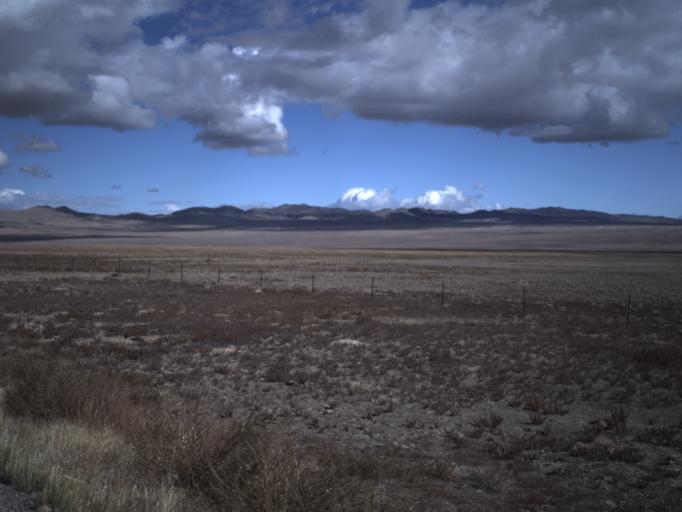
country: US
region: Utah
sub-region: Beaver County
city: Milford
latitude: 38.6677
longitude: -113.8824
